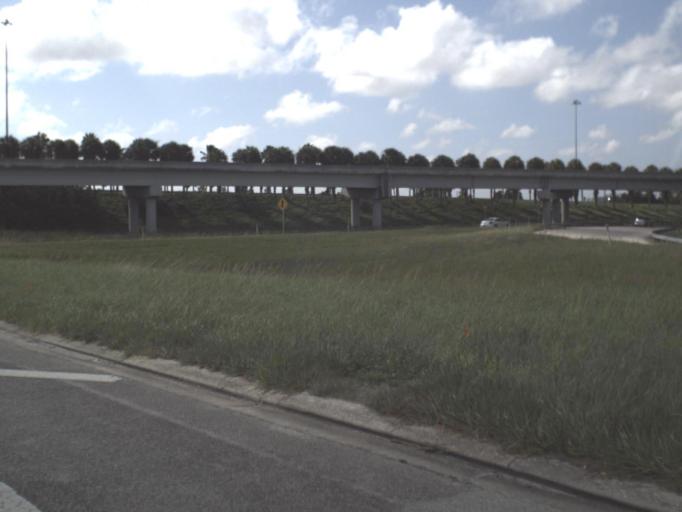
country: US
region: Florida
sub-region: Pinellas County
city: Feather Sound
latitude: 27.8797
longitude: -82.6603
